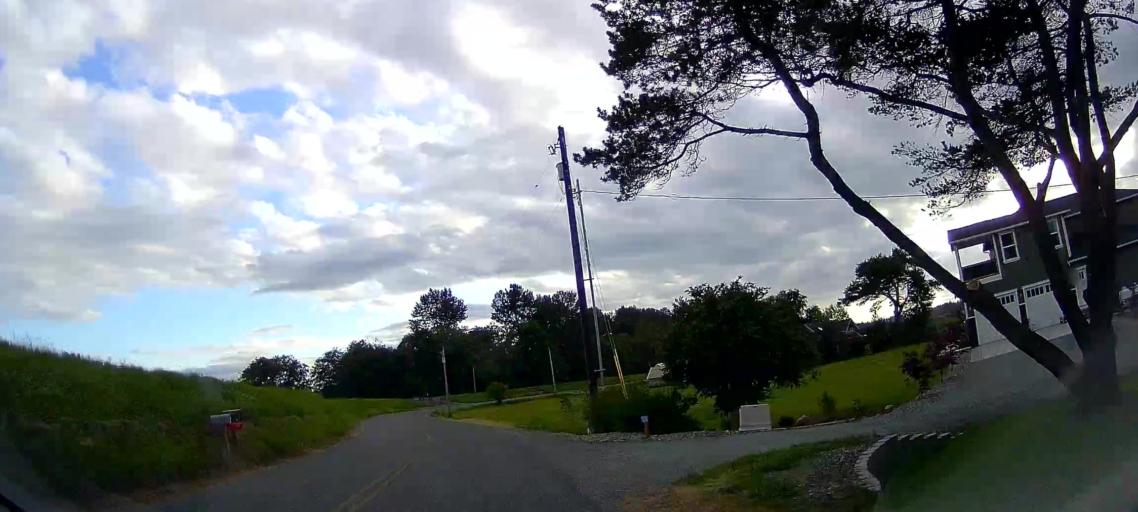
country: US
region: Washington
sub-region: Skagit County
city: Mount Vernon
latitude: 48.3679
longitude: -122.4078
